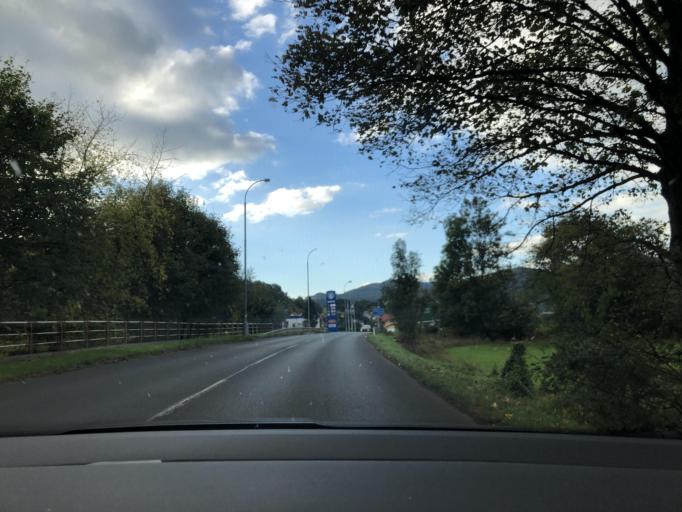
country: CZ
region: Ustecky
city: Velke Brezno
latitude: 50.6653
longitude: 14.1322
